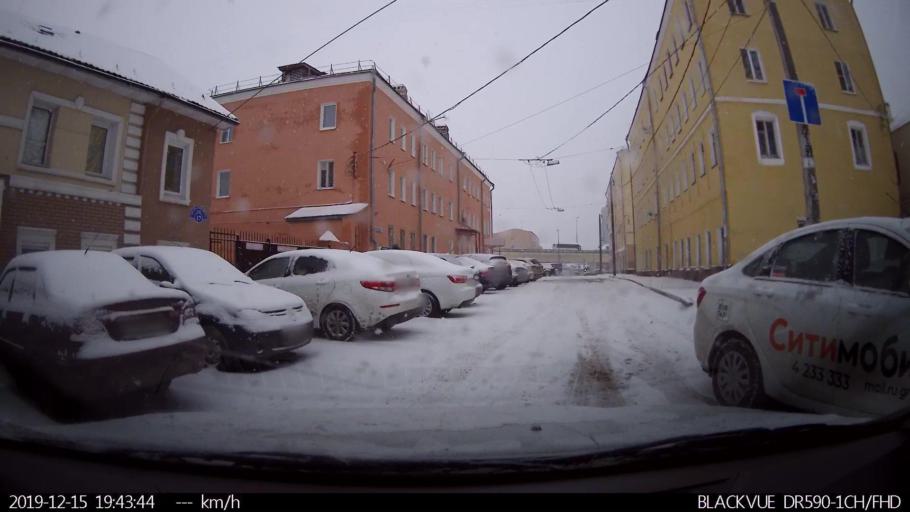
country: RU
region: Nizjnij Novgorod
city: Nizhniy Novgorod
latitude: 56.2955
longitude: 43.9731
